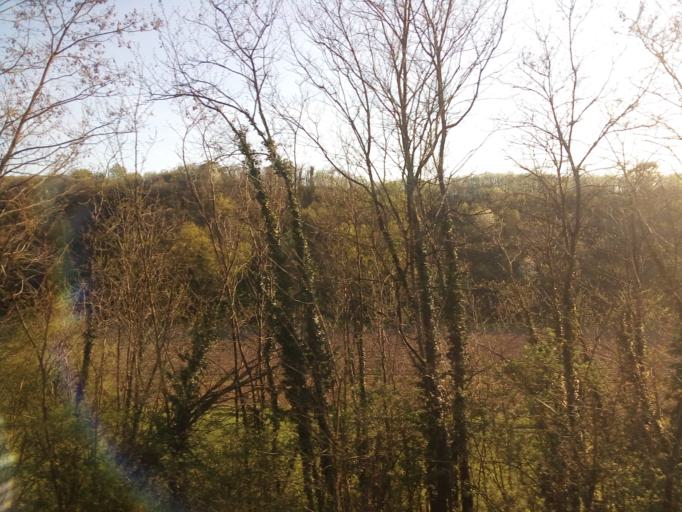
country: FR
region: Rhone-Alpes
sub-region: Departement de l'Isere
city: Saint-Didier-de-la-Tour
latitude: 45.5560
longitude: 5.5084
